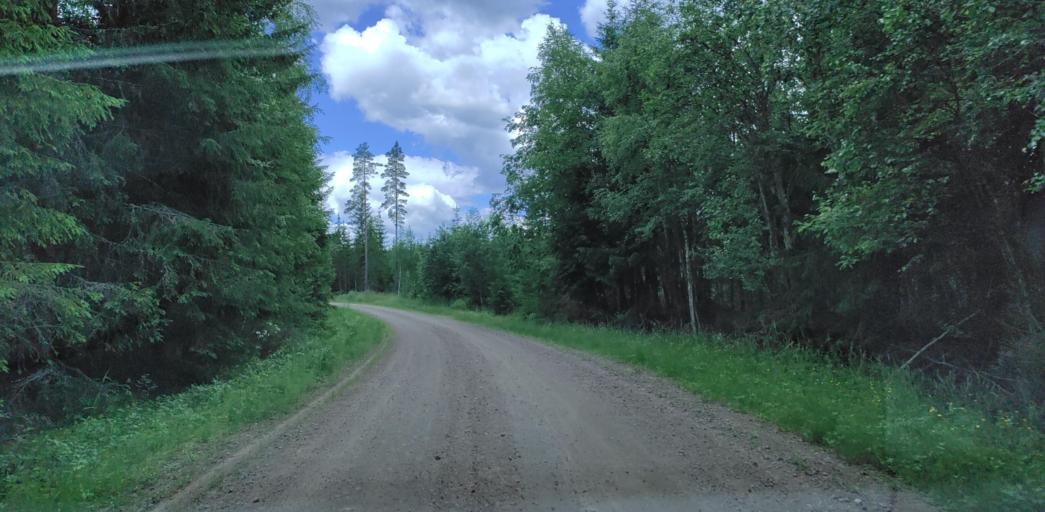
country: SE
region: Vaermland
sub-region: Hagfors Kommun
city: Ekshaerad
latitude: 60.0874
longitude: 13.4365
